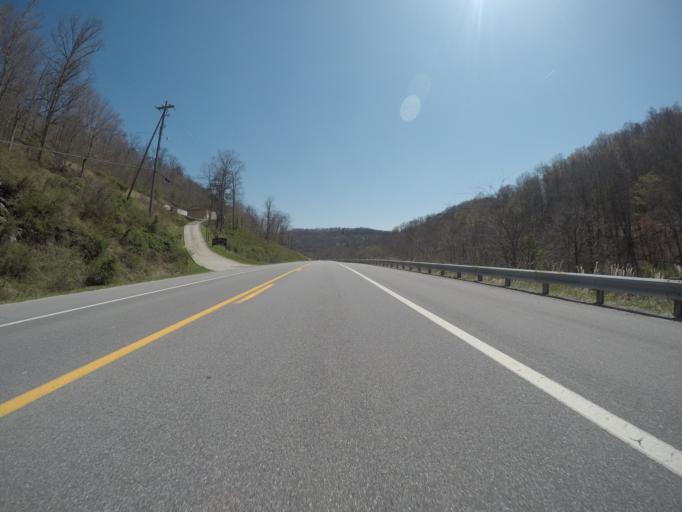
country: US
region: West Virginia
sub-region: Kanawha County
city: Pinch
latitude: 38.4129
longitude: -81.5451
